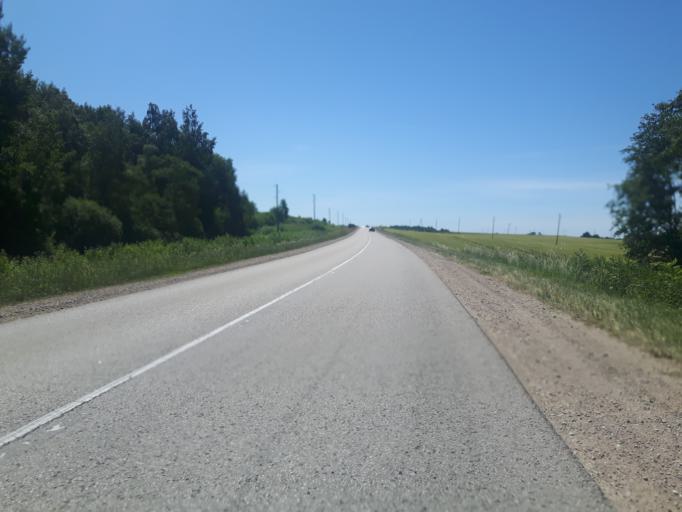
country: LV
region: Durbe
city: Liegi
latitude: 56.5872
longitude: 21.2707
